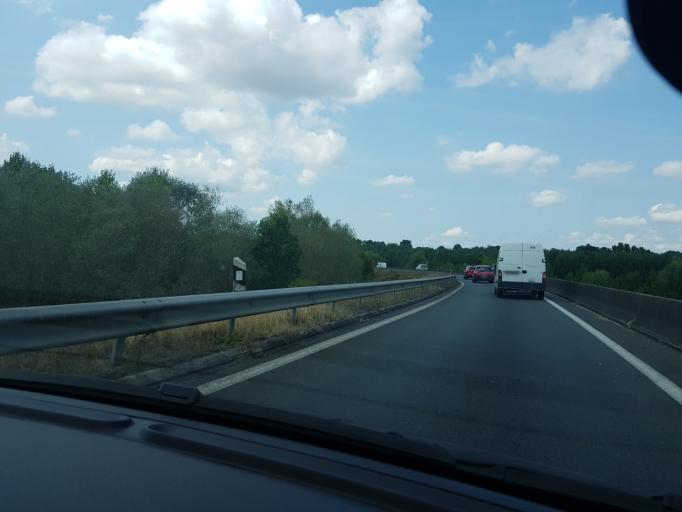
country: FR
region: Aquitaine
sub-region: Departement de la Gironde
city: Arveyres
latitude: 44.8726
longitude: -0.2810
